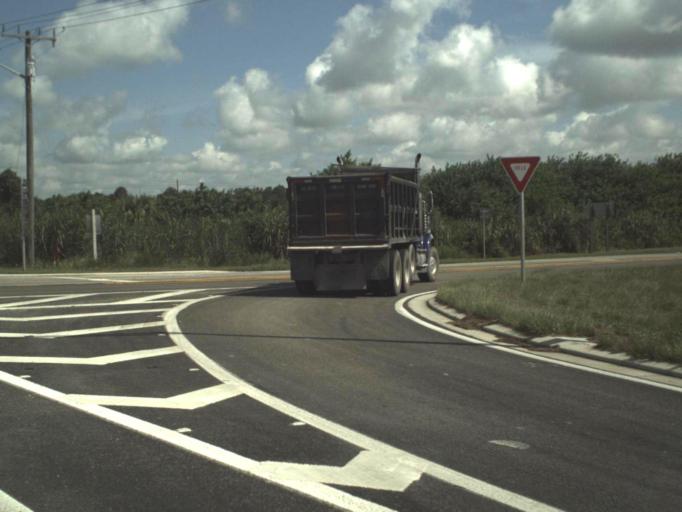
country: US
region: Florida
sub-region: Martin County
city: Indiantown
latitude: 27.0081
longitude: -80.4489
